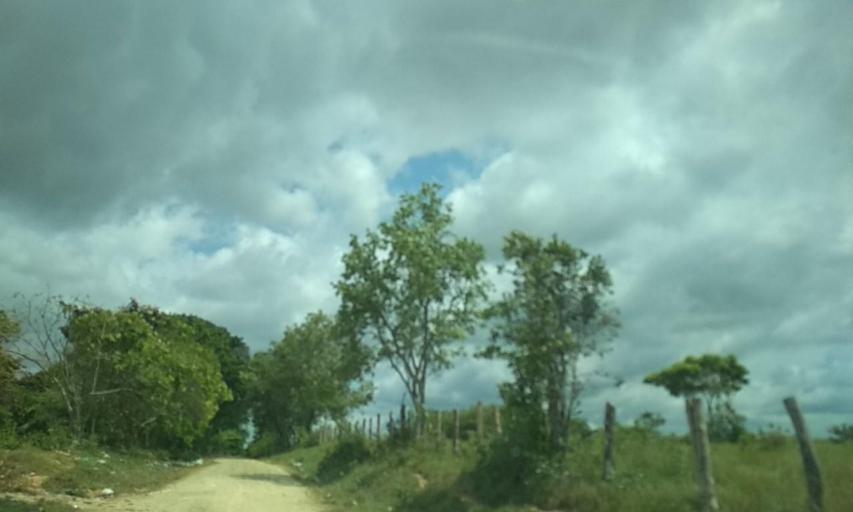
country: MX
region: Veracruz
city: Las Choapas
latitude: 17.8947
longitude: -94.1175
